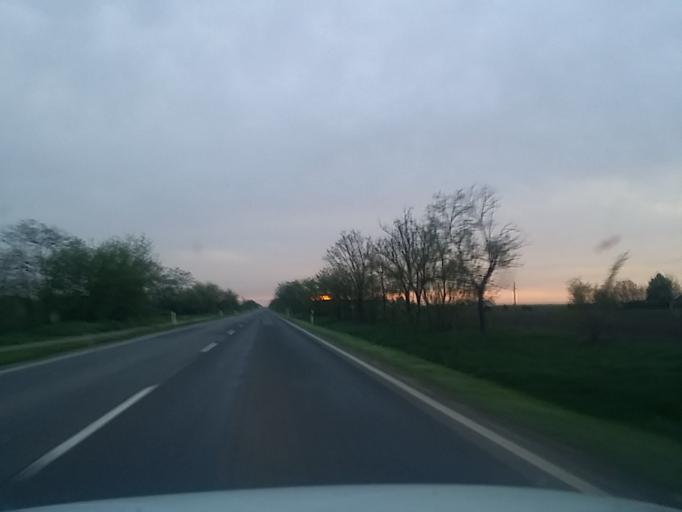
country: HU
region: Bekes
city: Mezobereny
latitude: 46.7093
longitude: 20.9836
